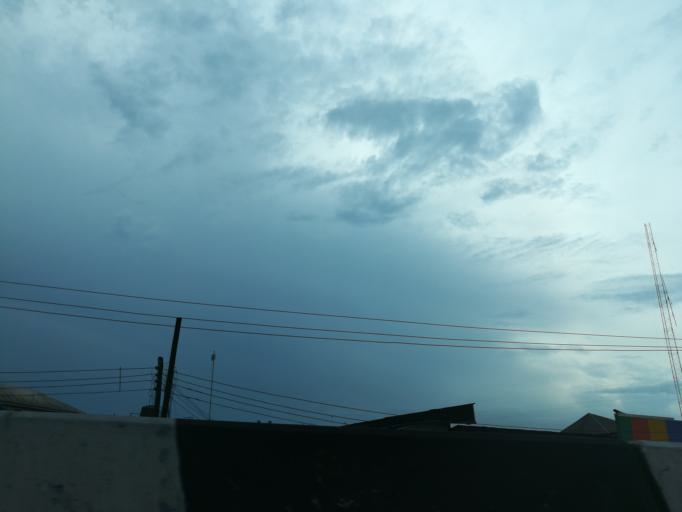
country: NG
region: Rivers
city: Port Harcourt
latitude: 4.7984
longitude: 7.0058
